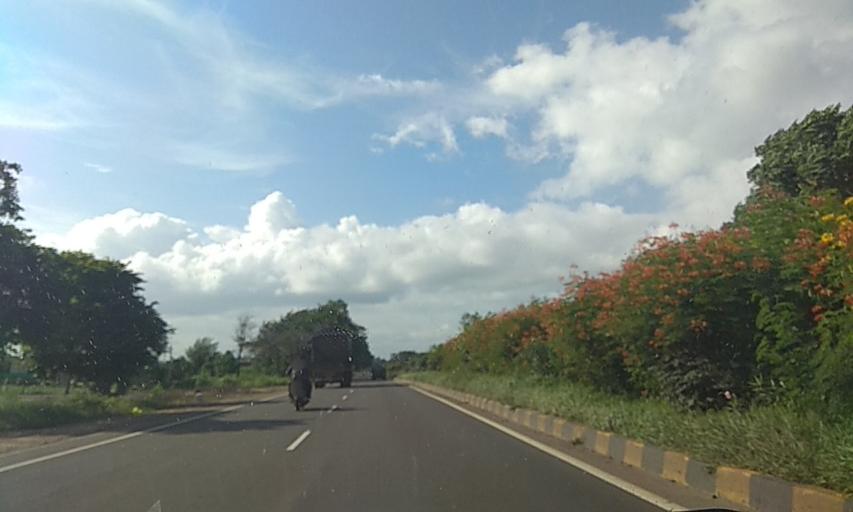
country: IN
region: Maharashtra
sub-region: Kolhapur
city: Kodoli
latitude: 17.0268
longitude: 74.2482
